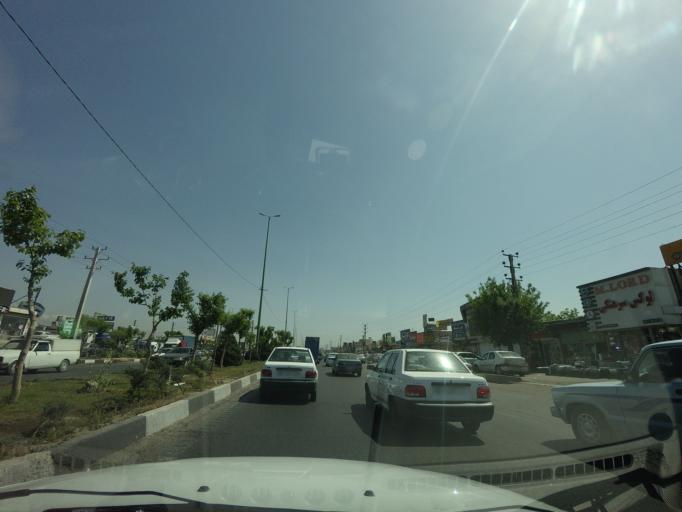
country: IR
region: Tehran
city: Eslamshahr
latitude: 35.5857
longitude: 51.2806
